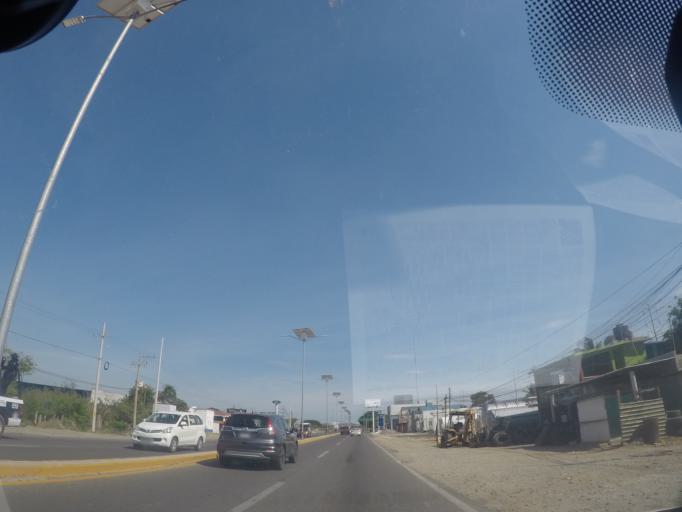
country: MX
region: Oaxaca
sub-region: Santo Domingo Tehuantepec
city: La Noria
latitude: 16.2253
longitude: -95.2096
